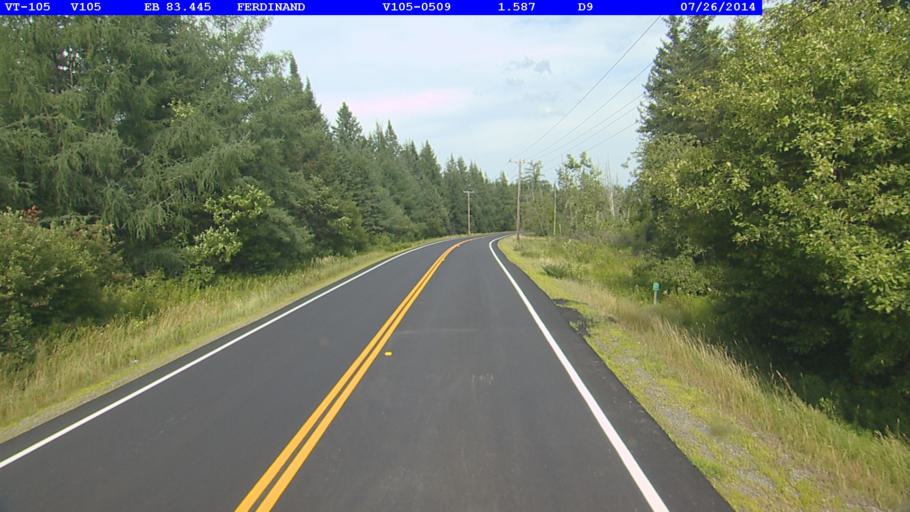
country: US
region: New Hampshire
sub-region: Coos County
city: Stratford
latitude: 44.7801
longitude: -71.7732
